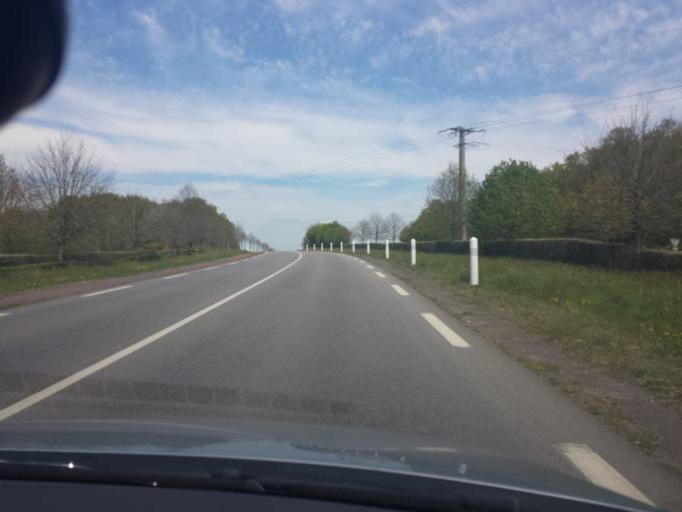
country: FR
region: Haute-Normandie
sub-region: Departement de l'Eure
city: Breteuil
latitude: 48.8200
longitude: 0.9236
